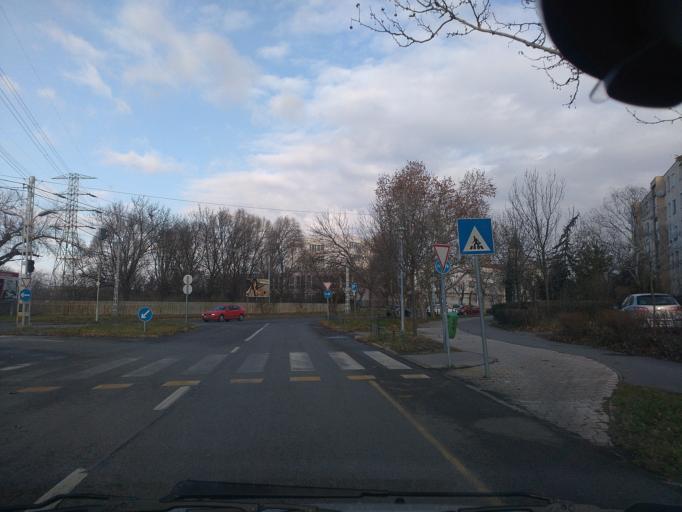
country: HU
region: Budapest
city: Budapest XX. keruelet
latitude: 47.4688
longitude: 19.1079
